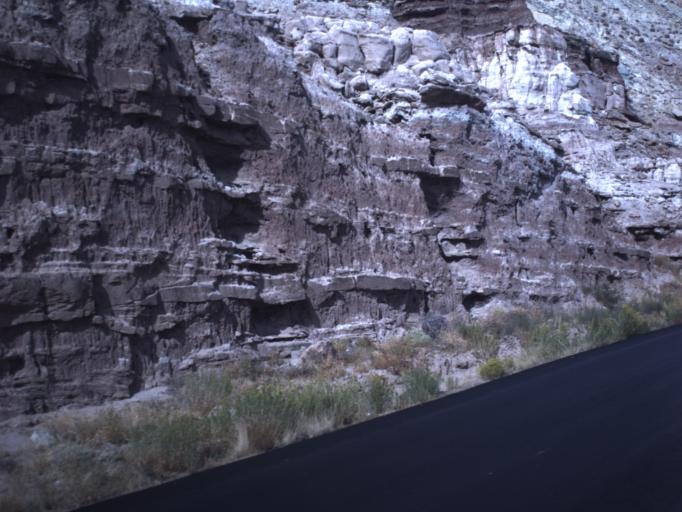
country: US
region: Utah
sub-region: San Juan County
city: Blanding
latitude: 37.2579
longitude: -109.2774
